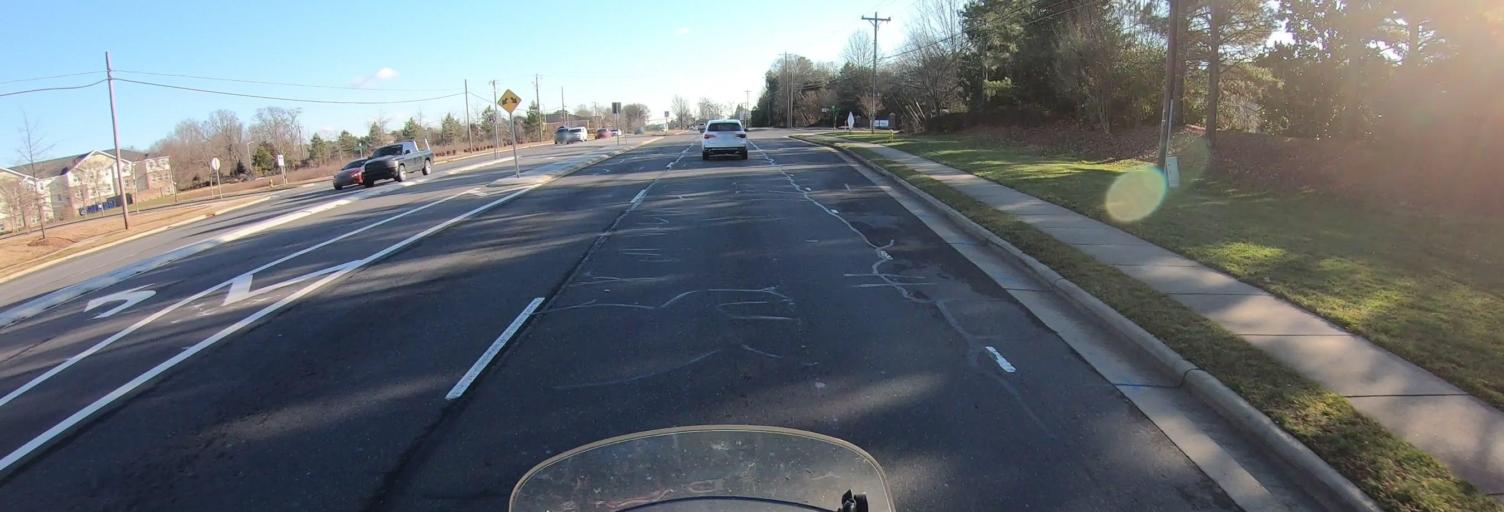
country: US
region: South Carolina
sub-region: York County
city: Lake Wylie
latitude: 35.1136
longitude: -80.9673
